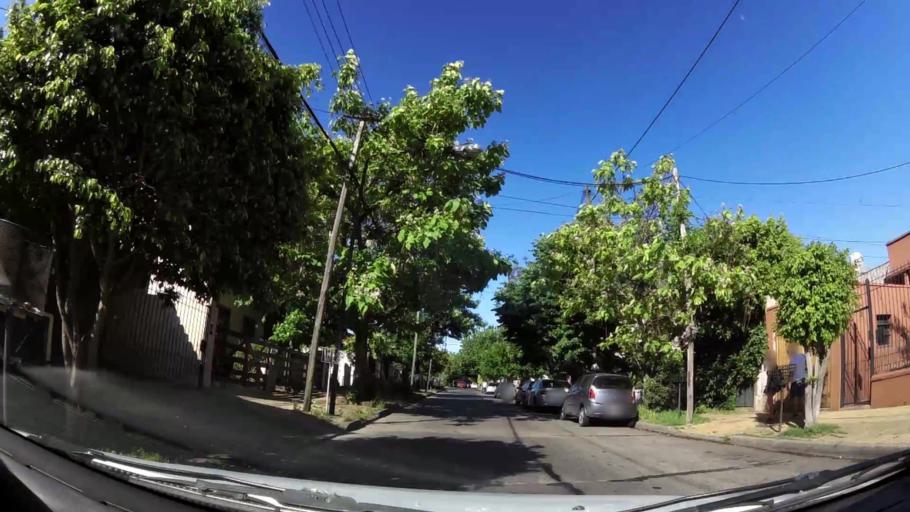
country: AR
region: Buenos Aires
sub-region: Partido de San Isidro
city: San Isidro
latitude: -34.4761
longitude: -58.5272
